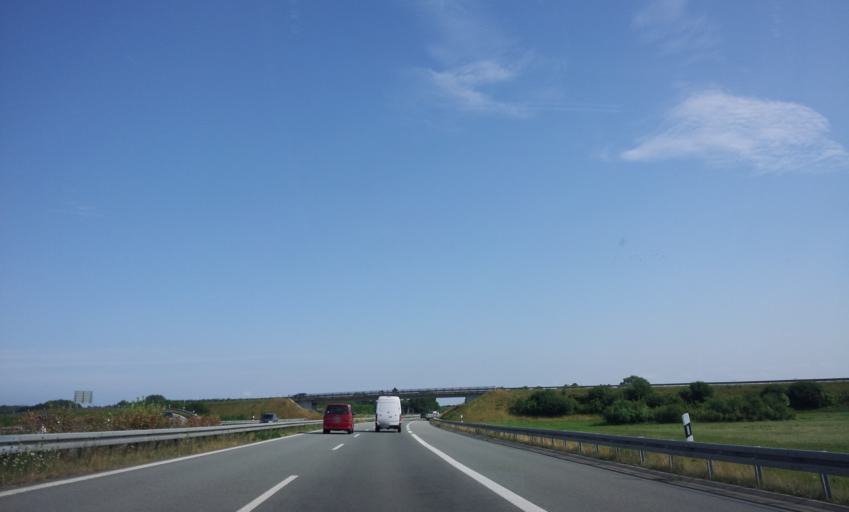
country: DE
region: Mecklenburg-Vorpommern
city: Brandshagen
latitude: 54.2404
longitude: 13.1447
